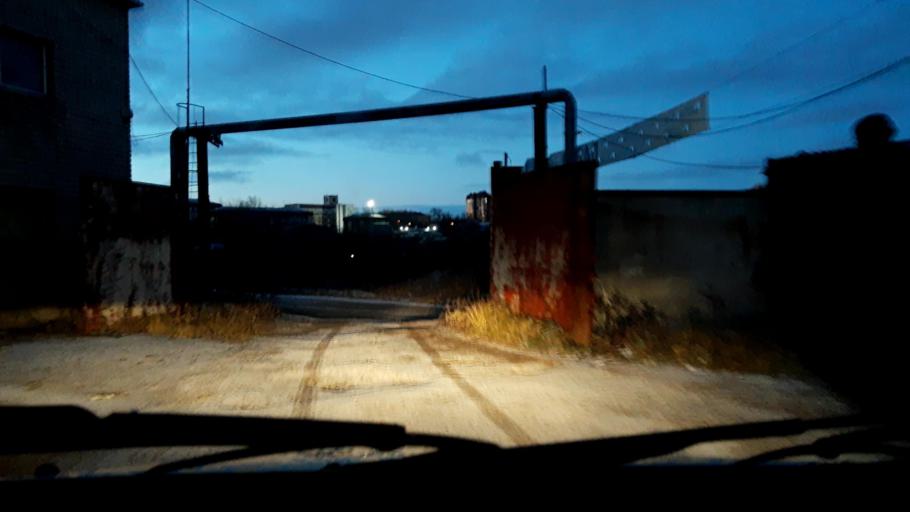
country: RU
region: Bashkortostan
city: Ufa
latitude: 54.8304
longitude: 56.0824
